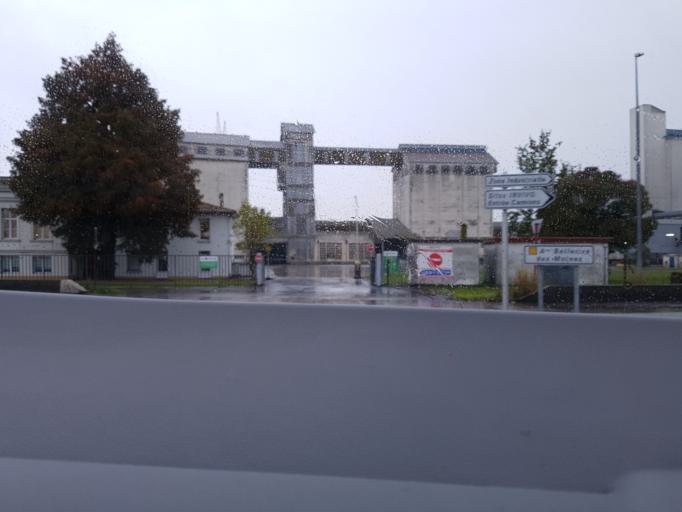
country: FR
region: Aquitaine
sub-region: Departement de la Gironde
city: Bassens
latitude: 44.9151
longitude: -0.5416
